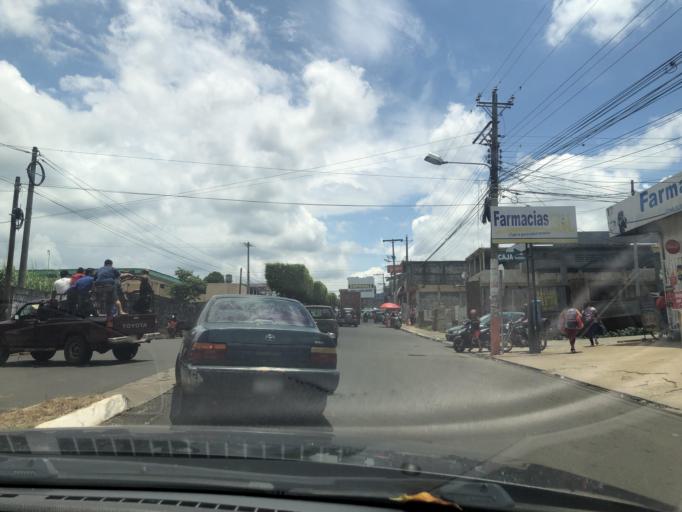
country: GT
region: Quetzaltenango
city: Coatepeque
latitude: 14.7046
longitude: -91.8681
